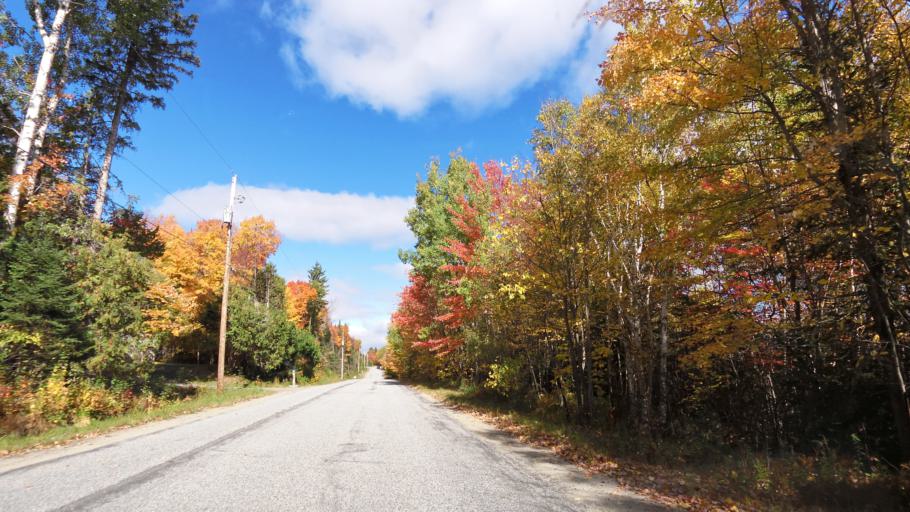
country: CA
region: Ontario
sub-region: Nipissing District
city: North Bay
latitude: 46.3728
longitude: -79.4871
